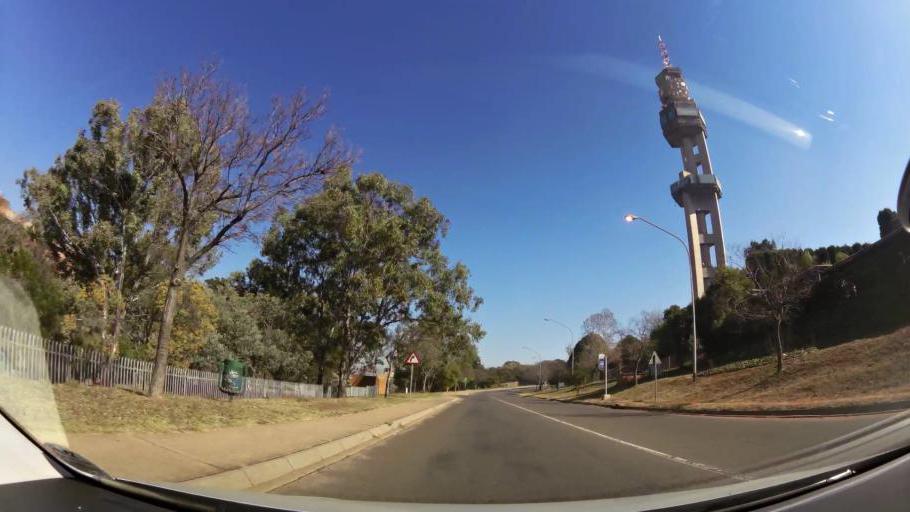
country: ZA
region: Gauteng
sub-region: City of Tshwane Metropolitan Municipality
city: Pretoria
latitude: -25.7672
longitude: 28.2074
